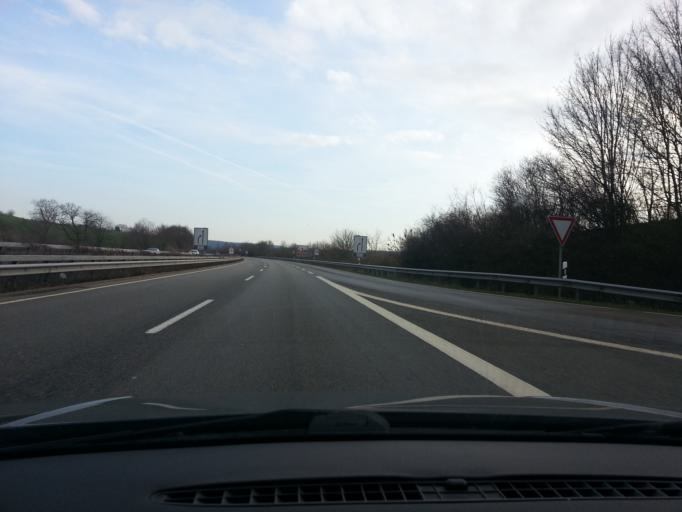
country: DE
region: Rheinland-Pfalz
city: Walshausen
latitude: 49.2147
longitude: 7.4987
